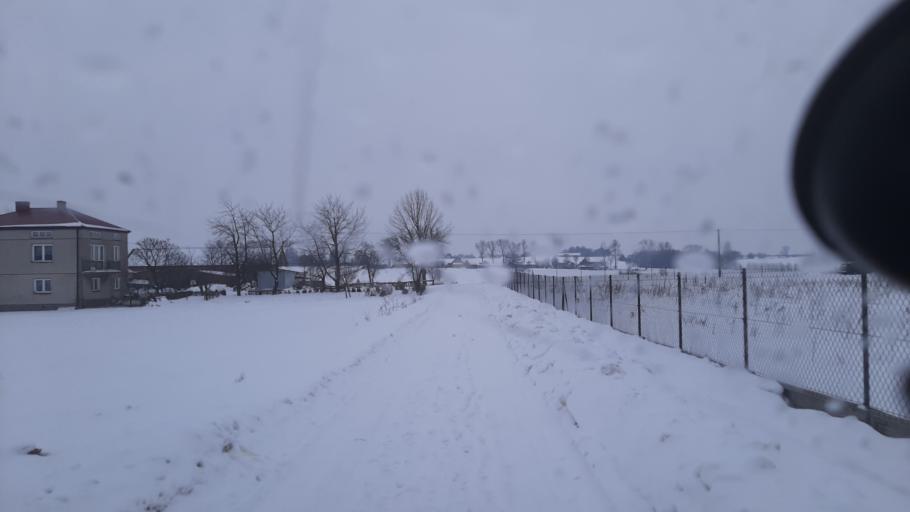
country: PL
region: Lublin Voivodeship
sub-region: Powiat lubelski
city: Jastkow
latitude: 51.3504
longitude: 22.4001
